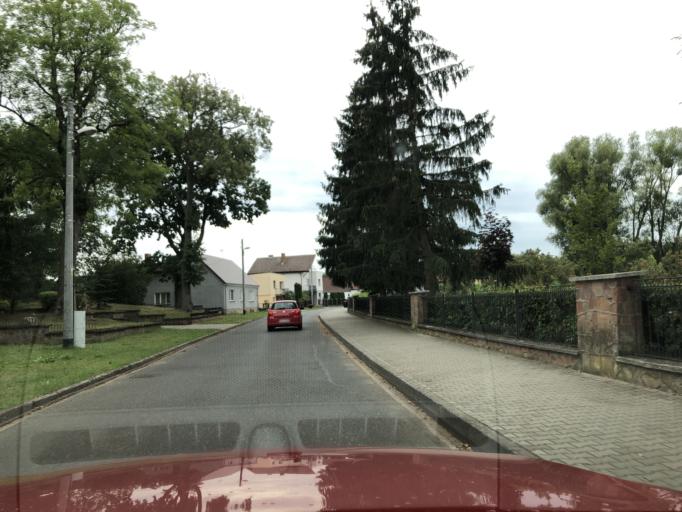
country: PL
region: Greater Poland Voivodeship
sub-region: Powiat szamotulski
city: Pniewy
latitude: 52.5126
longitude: 16.2507
